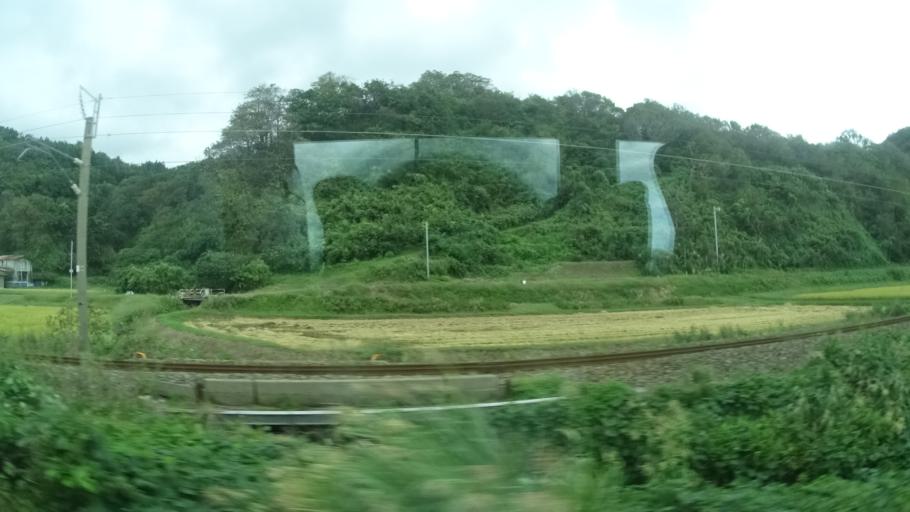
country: JP
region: Niigata
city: Murakami
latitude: 38.2578
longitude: 139.4465
